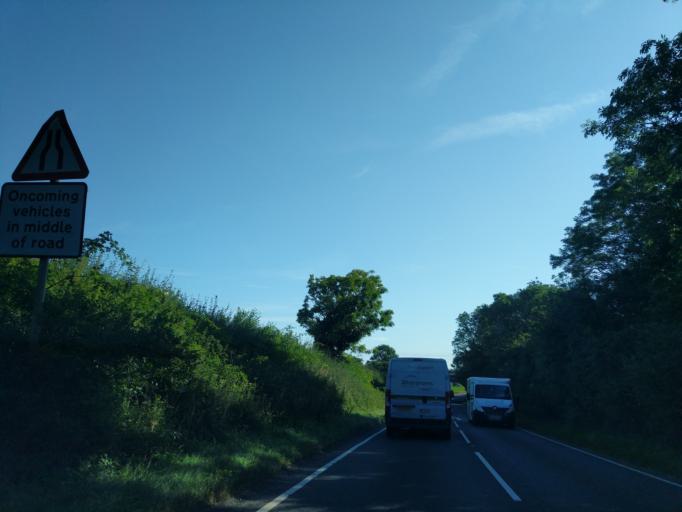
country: GB
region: England
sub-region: District of Rutland
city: Clipsham
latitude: 52.8084
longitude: -0.5421
